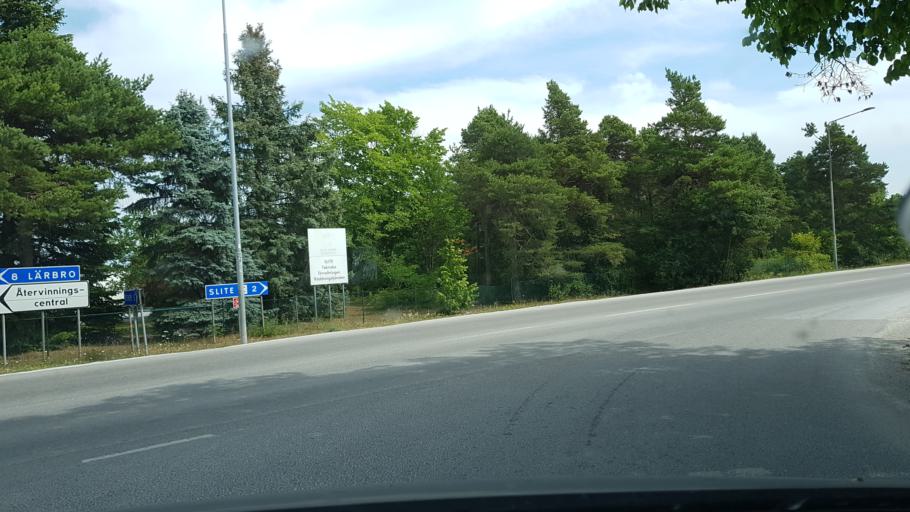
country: SE
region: Gotland
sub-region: Gotland
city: Slite
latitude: 57.7211
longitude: 18.7898
